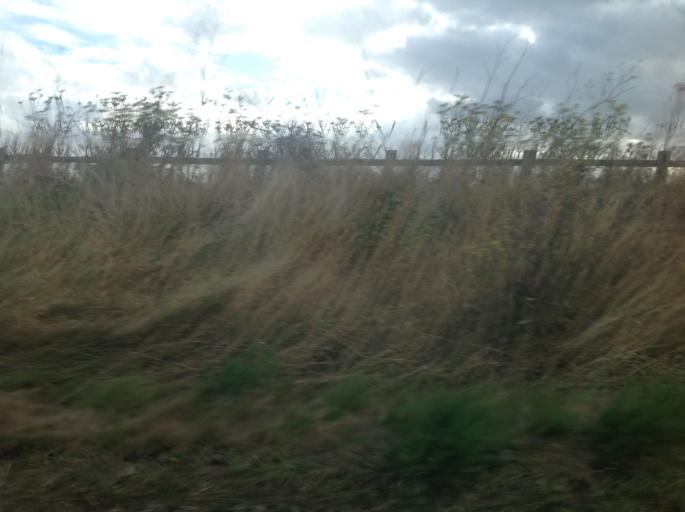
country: GB
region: England
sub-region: Suffolk
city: Kesgrave
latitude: 52.0200
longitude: 1.2646
